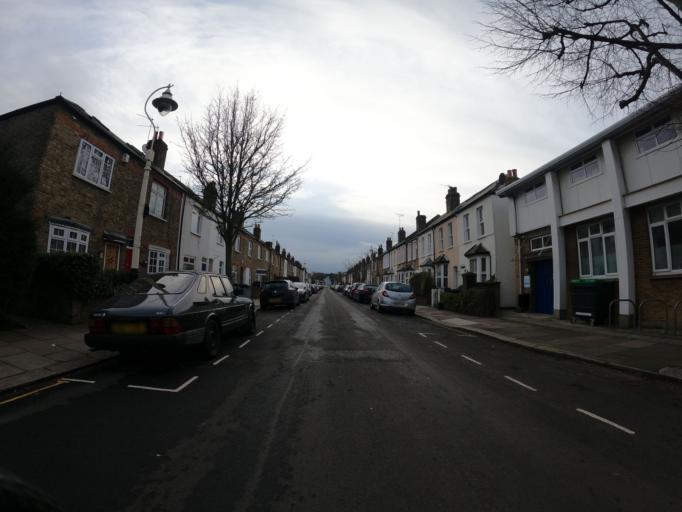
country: GB
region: England
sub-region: Greater London
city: Brentford
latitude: 51.5002
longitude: -0.3187
